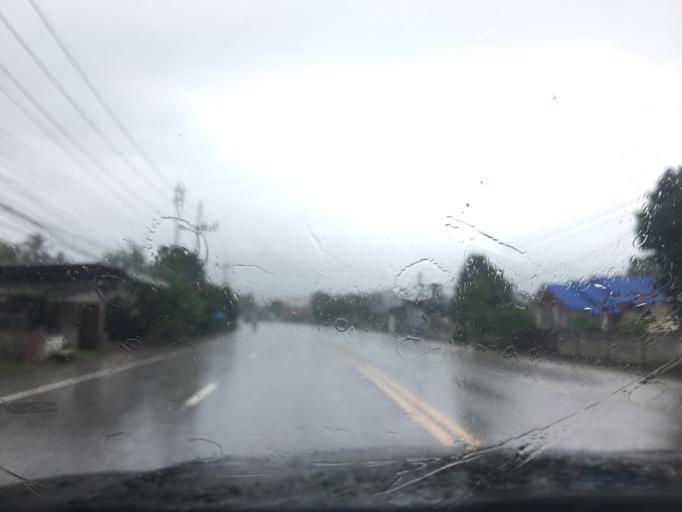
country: TH
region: Chiang Rai
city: Chiang Saen
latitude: 20.2986
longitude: 100.2319
